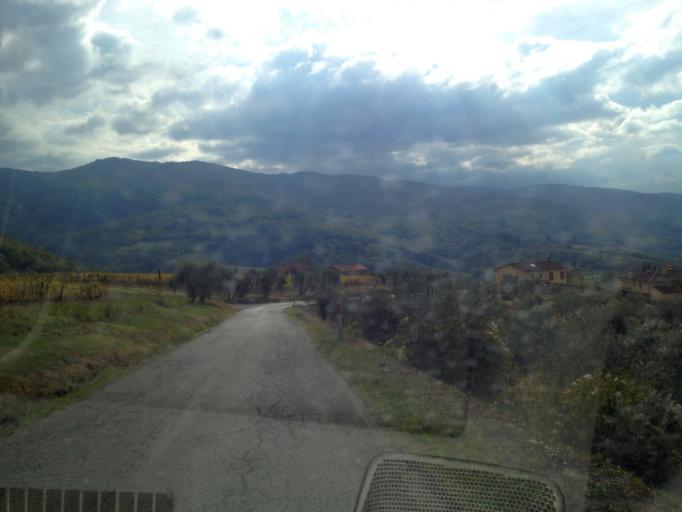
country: IT
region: Tuscany
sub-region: Province of Florence
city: Montebonello
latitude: 43.8566
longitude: 11.5002
